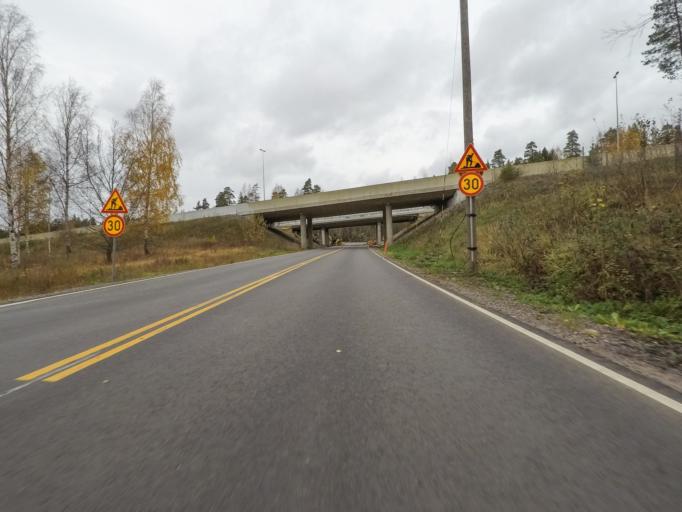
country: FI
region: Uusimaa
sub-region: Porvoo
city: Porvoo
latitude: 60.4161
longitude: 25.6727
